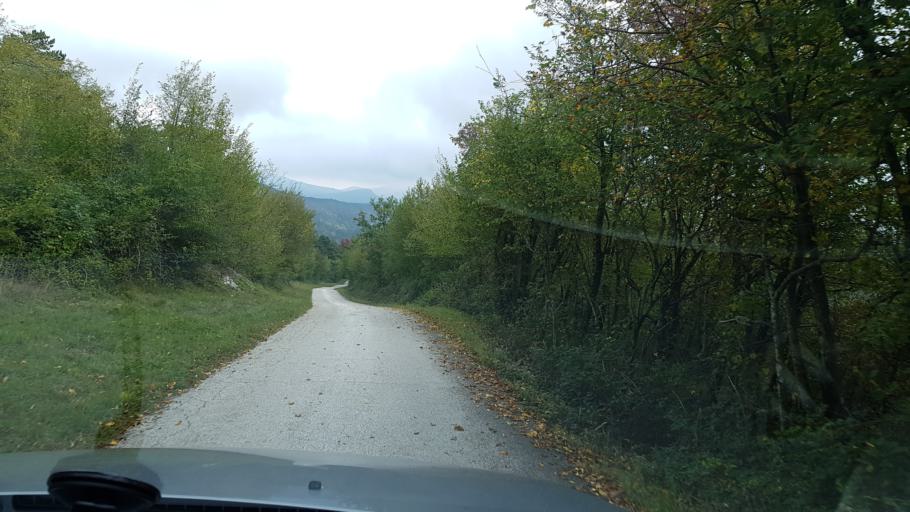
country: HR
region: Istarska
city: Buzet
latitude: 45.4486
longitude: 14.0262
